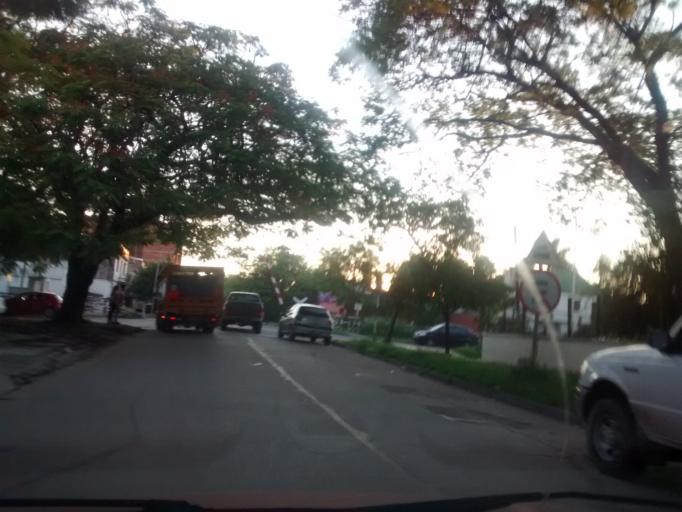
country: AR
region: Chaco
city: Resistencia
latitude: -27.4524
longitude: -58.9931
